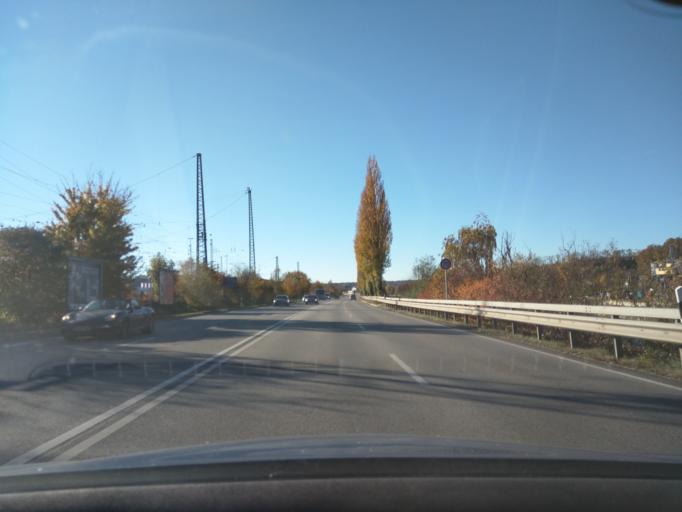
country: DE
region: Bavaria
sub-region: Lower Bavaria
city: Passau
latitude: 48.5734
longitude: 13.4359
